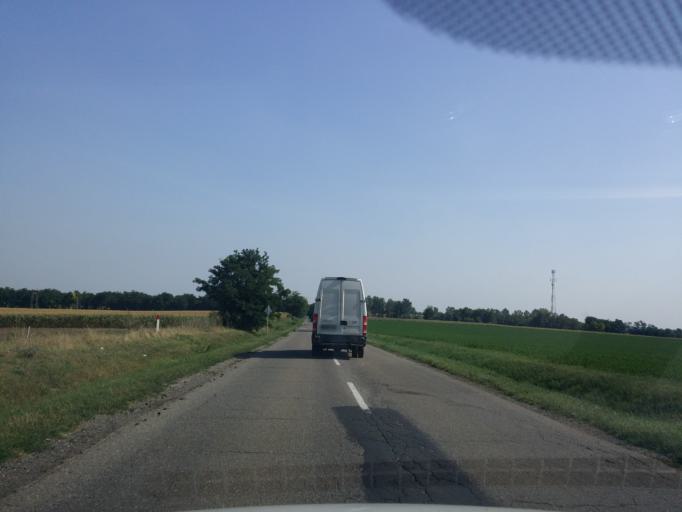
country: HU
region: Fejer
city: Mezofalva
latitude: 46.9393
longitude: 18.7490
